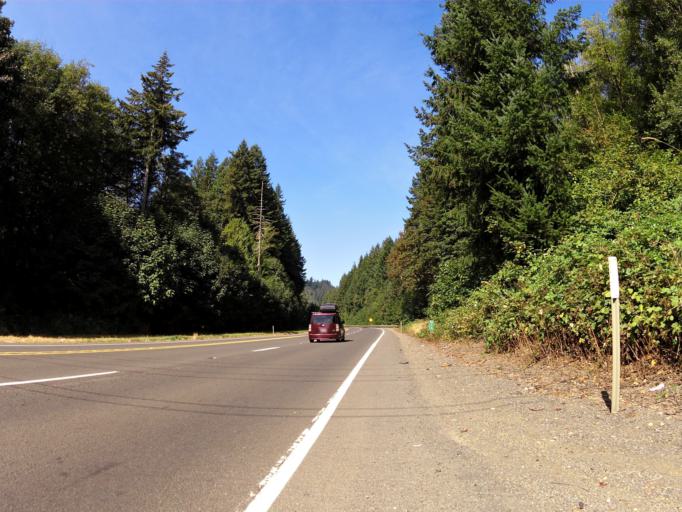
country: US
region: Washington
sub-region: Wahkiakum County
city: Cathlamet
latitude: 46.1528
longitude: -123.4136
